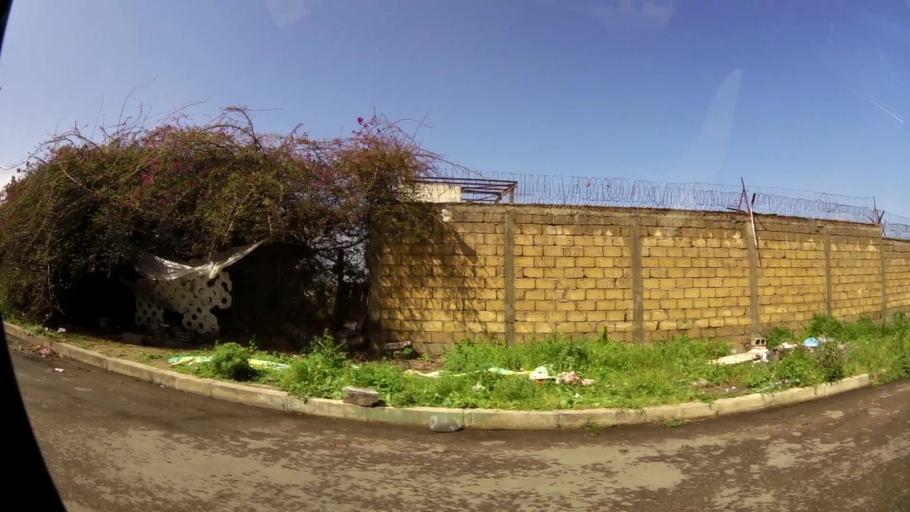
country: MA
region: Grand Casablanca
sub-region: Mediouna
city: Tit Mellil
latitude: 33.6190
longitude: -7.5093
